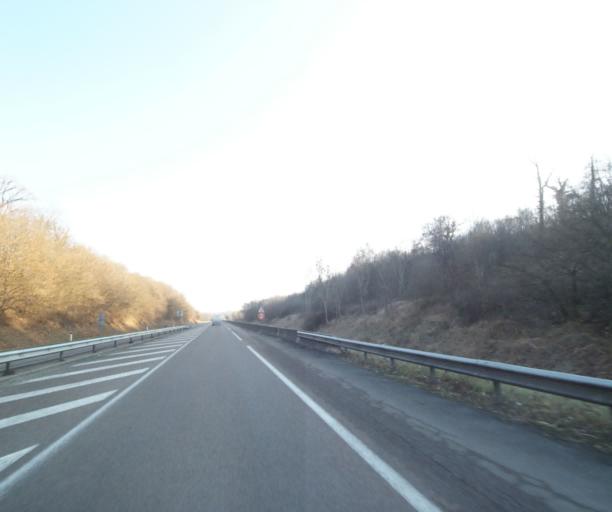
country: FR
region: Champagne-Ardenne
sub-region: Departement de la Haute-Marne
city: Chevillon
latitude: 48.5040
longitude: 5.1021
